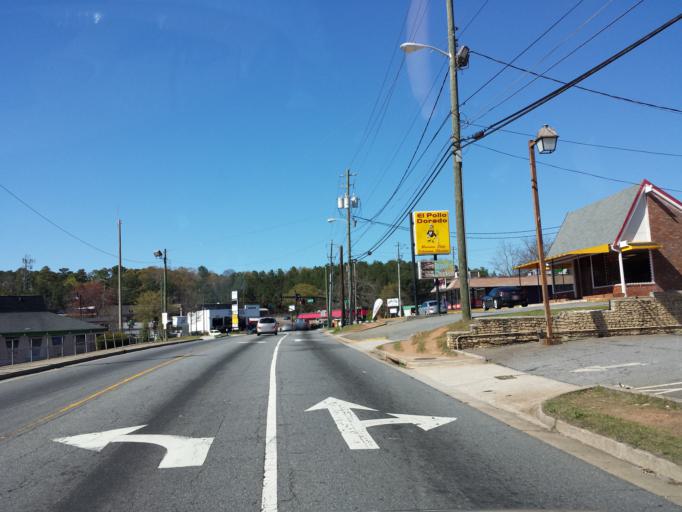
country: US
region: Georgia
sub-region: Cobb County
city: Marietta
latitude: 33.9349
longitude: -84.5558
